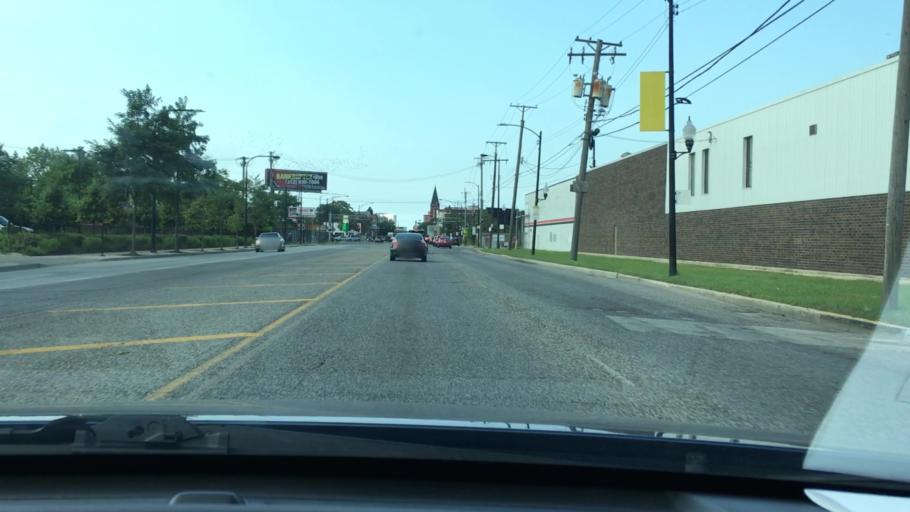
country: US
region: Illinois
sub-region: Cook County
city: Chicago
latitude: 41.8501
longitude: -87.6659
